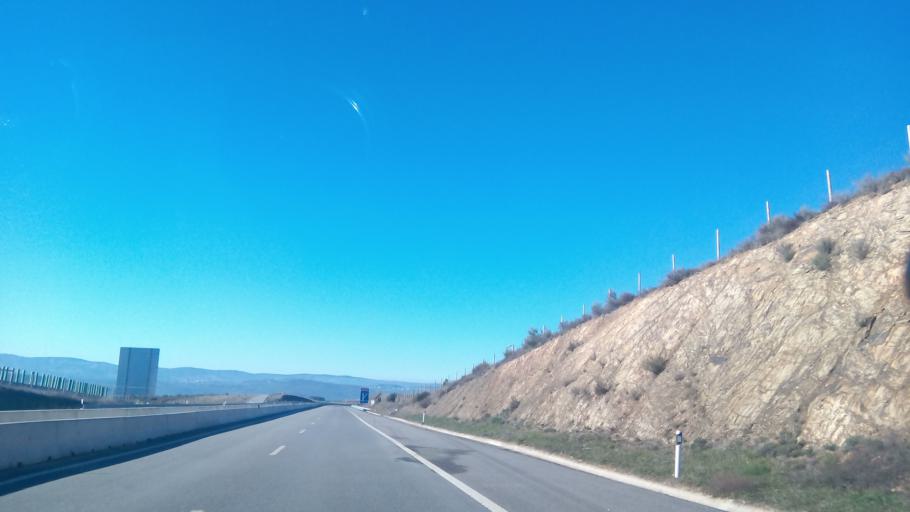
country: PT
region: Braganca
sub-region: Braganca Municipality
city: Braganca
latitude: 41.7546
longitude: -6.6356
